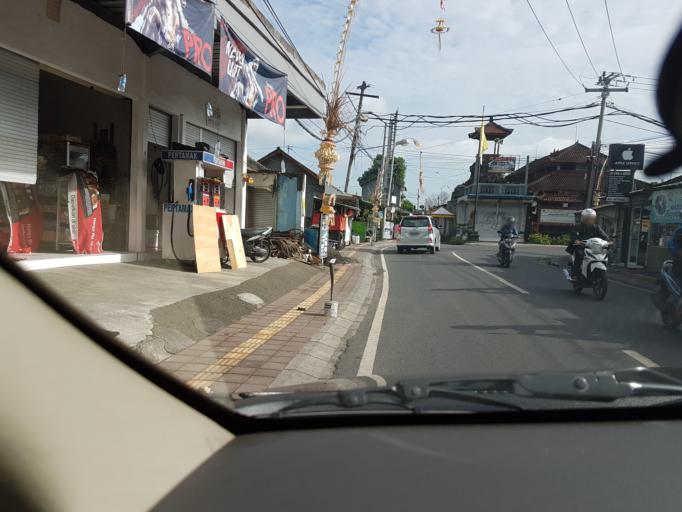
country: ID
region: Bali
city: Kuta
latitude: -8.6795
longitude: 115.1784
